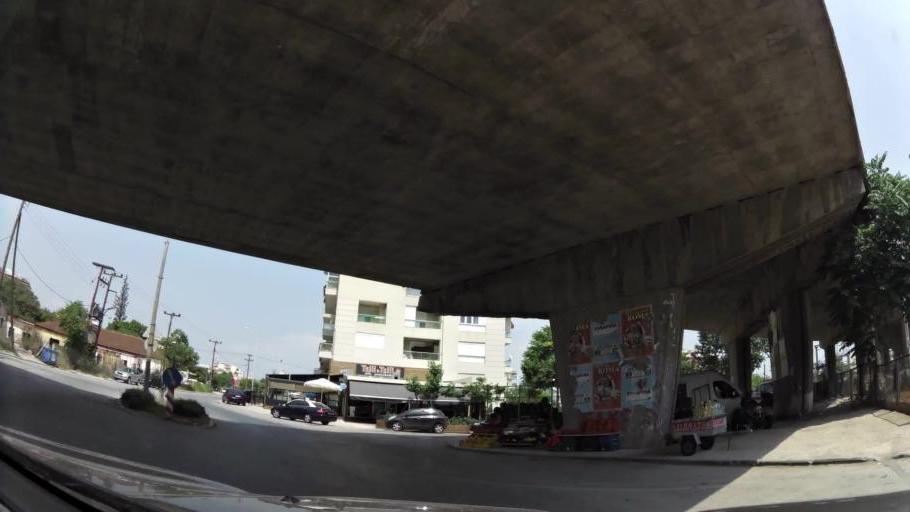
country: GR
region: Central Macedonia
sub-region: Nomos Thessalonikis
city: Menemeni
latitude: 40.6625
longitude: 22.8977
